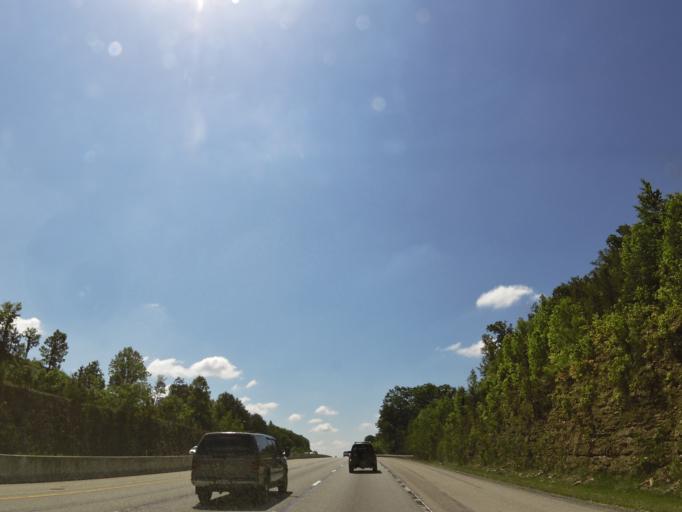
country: US
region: Kentucky
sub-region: Rockcastle County
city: Mount Vernon
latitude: 37.2954
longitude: -84.2745
